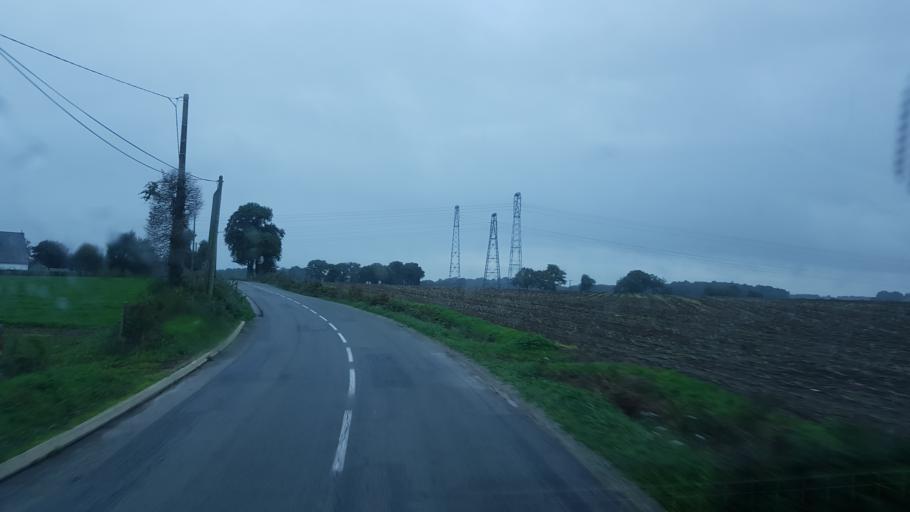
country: FR
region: Brittany
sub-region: Departement du Morbihan
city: Trefflean
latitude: 47.6596
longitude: -2.6256
